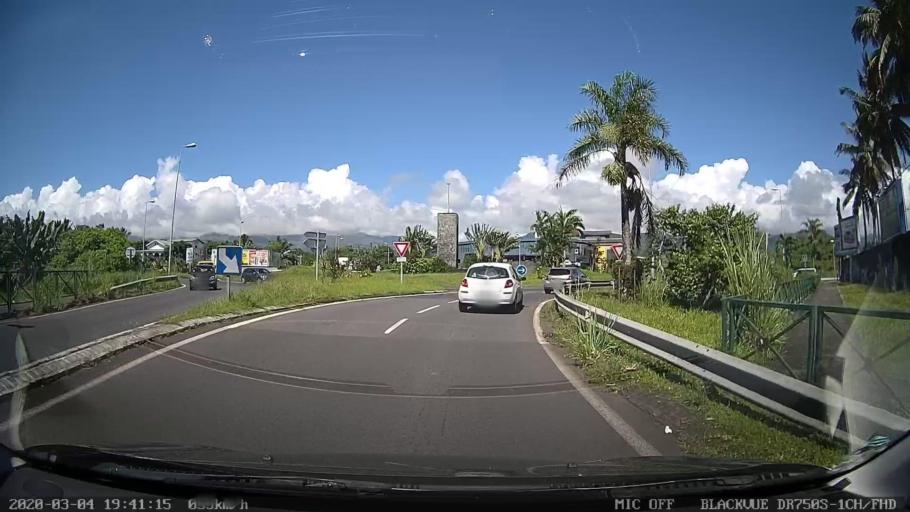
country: RE
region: Reunion
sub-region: Reunion
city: Saint-Benoit
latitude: -21.0474
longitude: 55.7177
